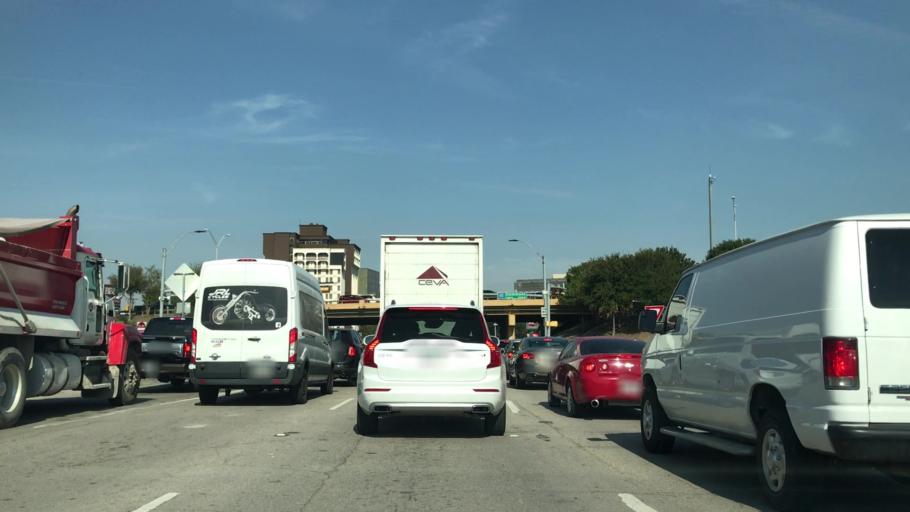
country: US
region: Texas
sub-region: Dallas County
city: Dallas
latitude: 32.8182
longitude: -96.8702
